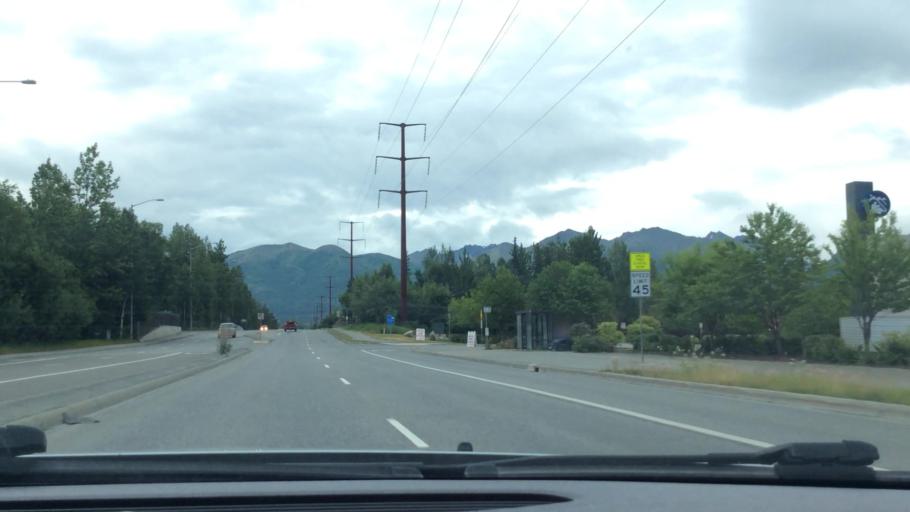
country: US
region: Alaska
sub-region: Anchorage Municipality
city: Anchorage
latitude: 61.1953
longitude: -149.7768
